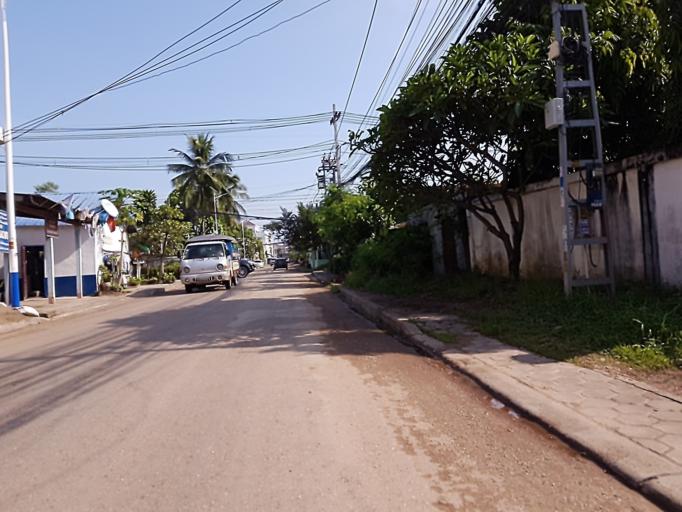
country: LA
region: Vientiane
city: Vientiane
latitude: 17.9527
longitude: 102.6256
